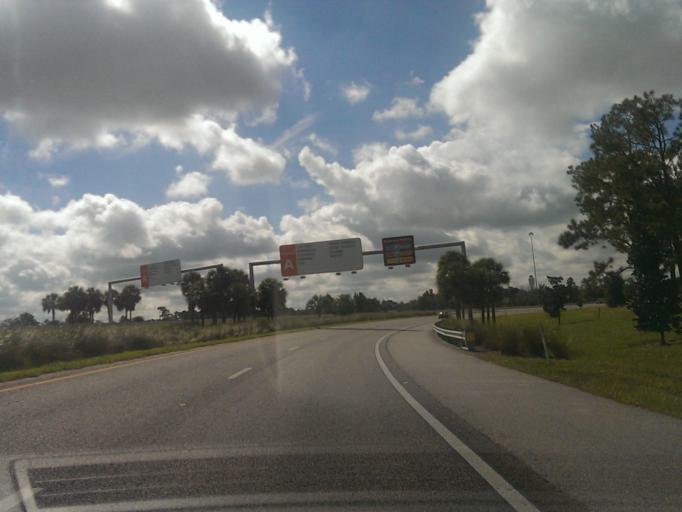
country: US
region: Florida
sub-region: Orange County
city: Belle Isle
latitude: 28.4479
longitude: -81.3096
